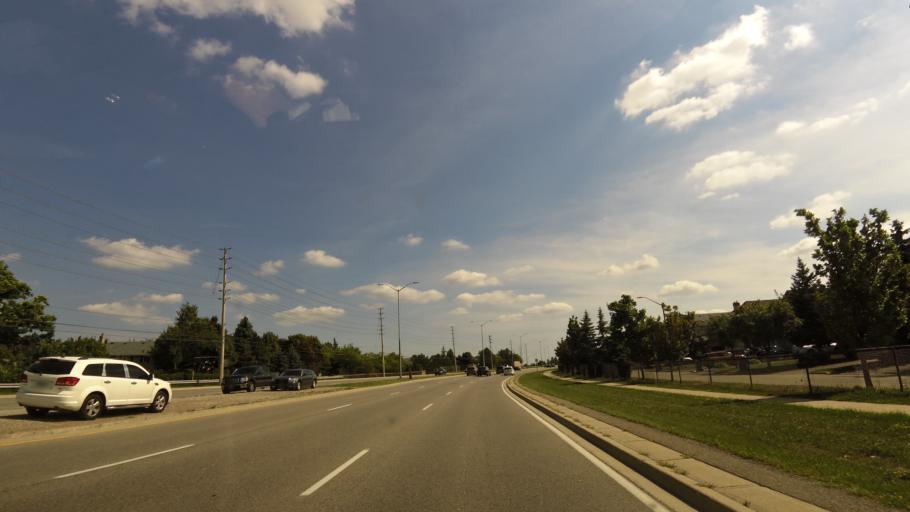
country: CA
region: Ontario
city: Mississauga
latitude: 43.5768
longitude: -79.7312
